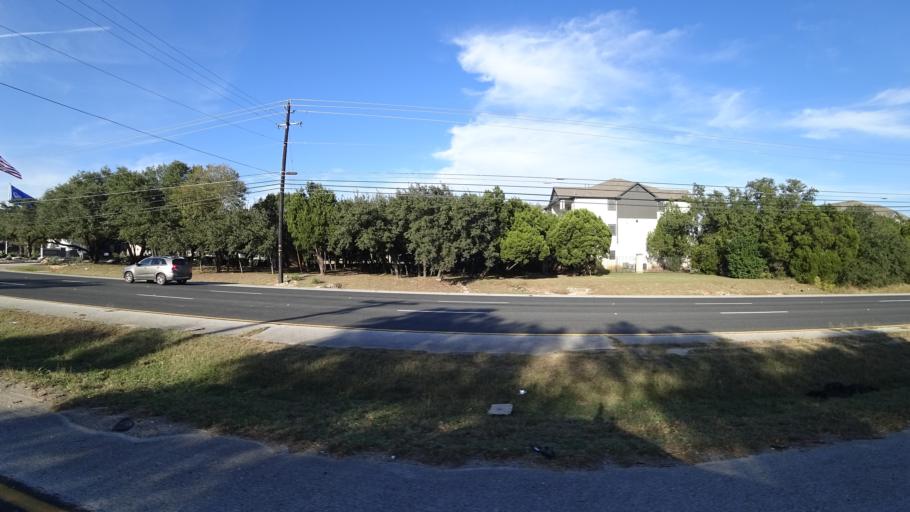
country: US
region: Texas
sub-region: Travis County
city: Barton Creek
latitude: 30.2462
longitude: -97.8462
